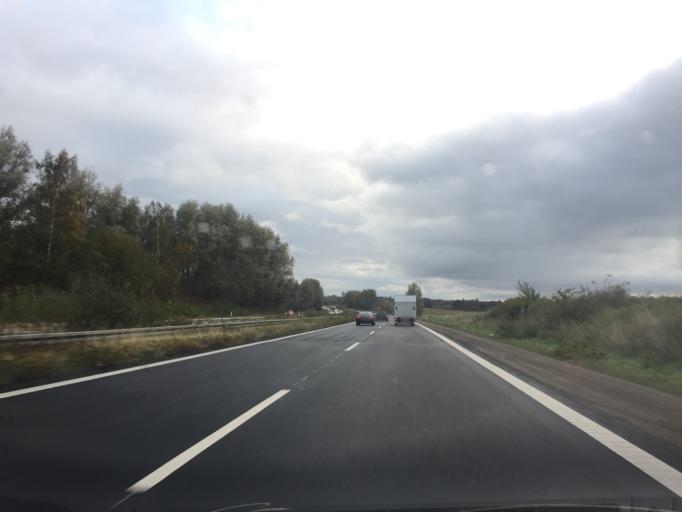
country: DK
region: Capital Region
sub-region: Fredensborg Kommune
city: Niva
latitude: 55.9514
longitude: 12.4786
